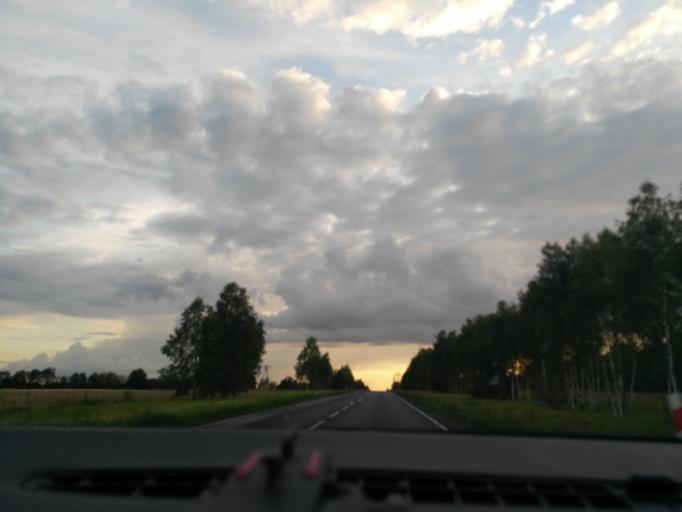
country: PL
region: Lublin Voivodeship
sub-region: Powiat lubartowski
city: Lubartow
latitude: 51.4354
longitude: 22.6187
